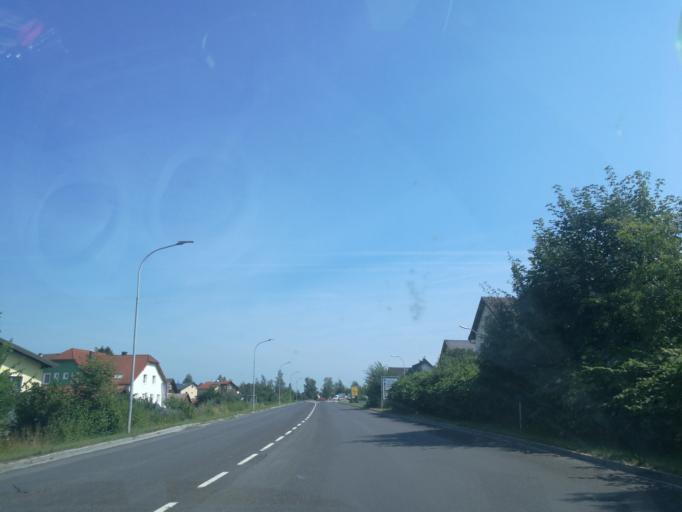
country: AT
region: Lower Austria
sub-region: Politischer Bezirk Gmund
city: Heidenreichstein
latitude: 48.8678
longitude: 15.1214
